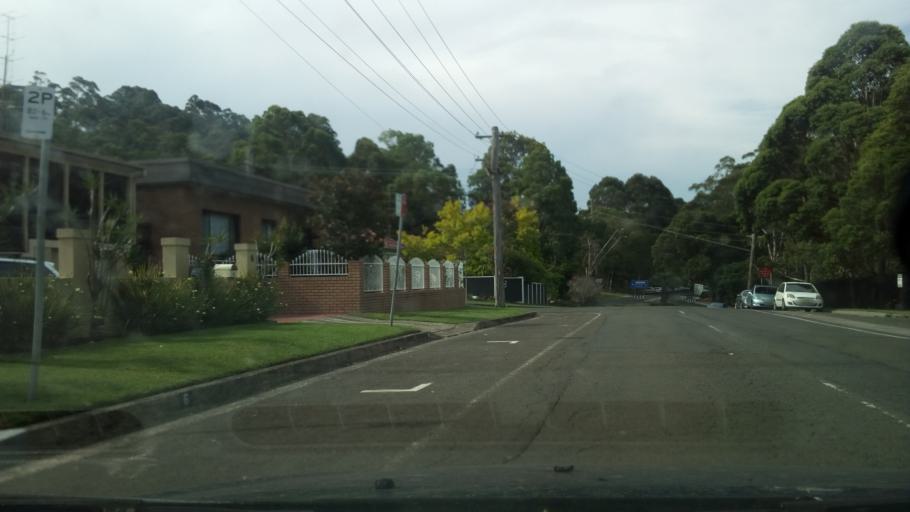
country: AU
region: New South Wales
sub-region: Wollongong
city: Mount Ousley
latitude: -34.4081
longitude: 150.8717
